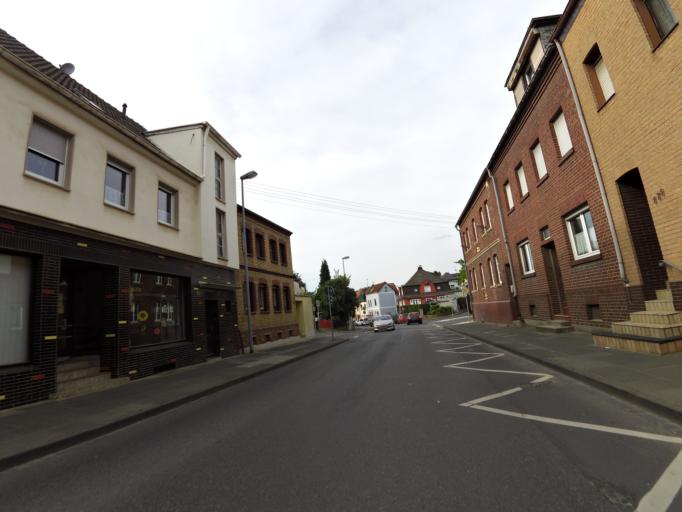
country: DE
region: North Rhine-Westphalia
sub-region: Regierungsbezirk Koln
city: Alfter
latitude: 50.6946
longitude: 7.0248
